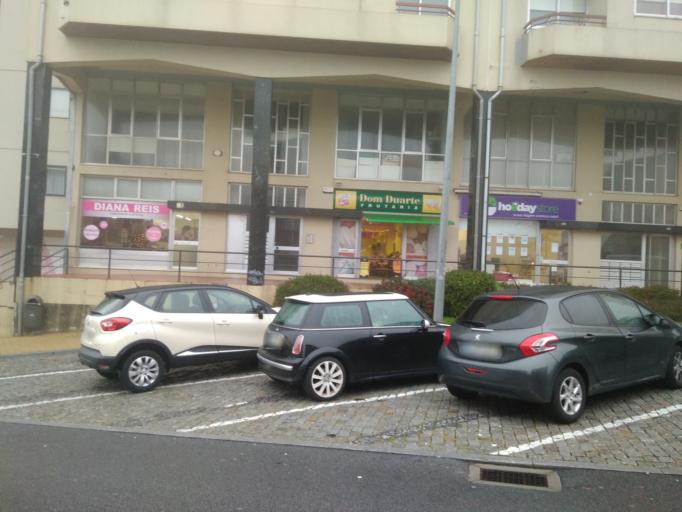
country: PT
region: Porto
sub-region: Vila Nova de Gaia
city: Vilar de Andorinho
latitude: 41.1154
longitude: -8.6079
